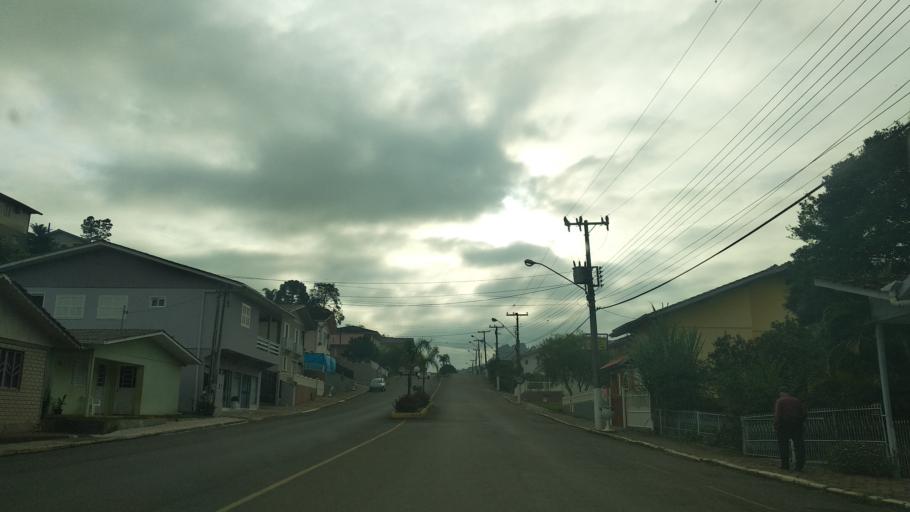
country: BR
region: Santa Catarina
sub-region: Videira
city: Videira
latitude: -27.0461
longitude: -51.2321
